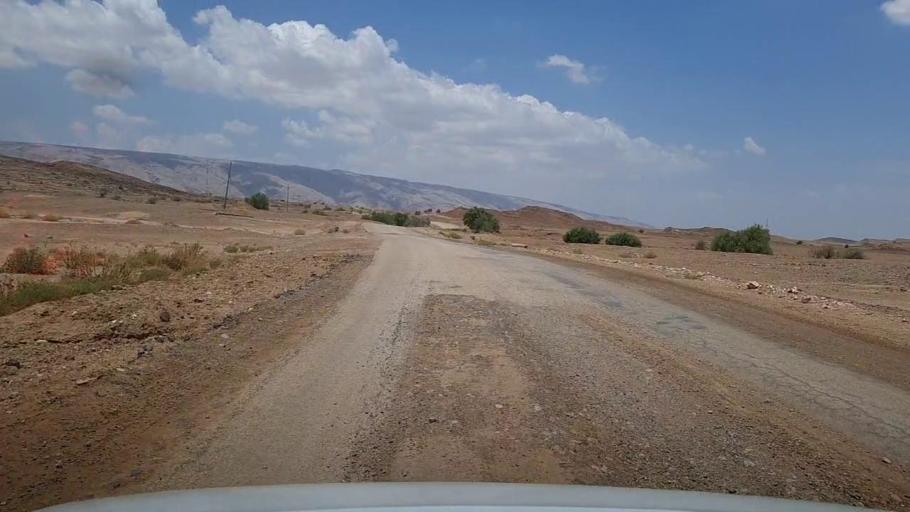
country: PK
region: Sindh
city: Bhan
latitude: 26.3176
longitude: 67.5616
